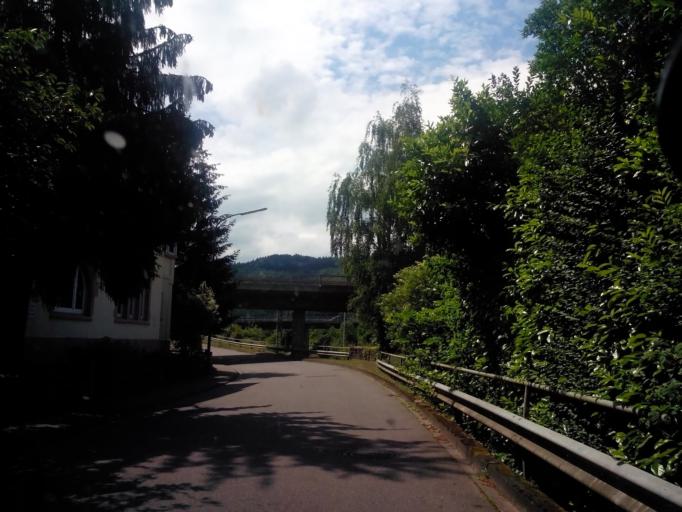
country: DE
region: Rheinland-Pfalz
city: Saarburg
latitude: 49.6044
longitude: 6.5562
